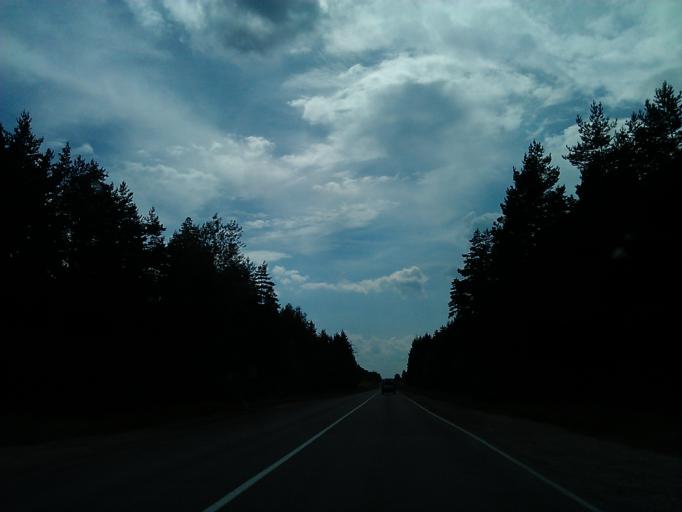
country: LV
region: Jaunpils
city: Jaunpils
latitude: 56.6860
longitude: 23.1110
